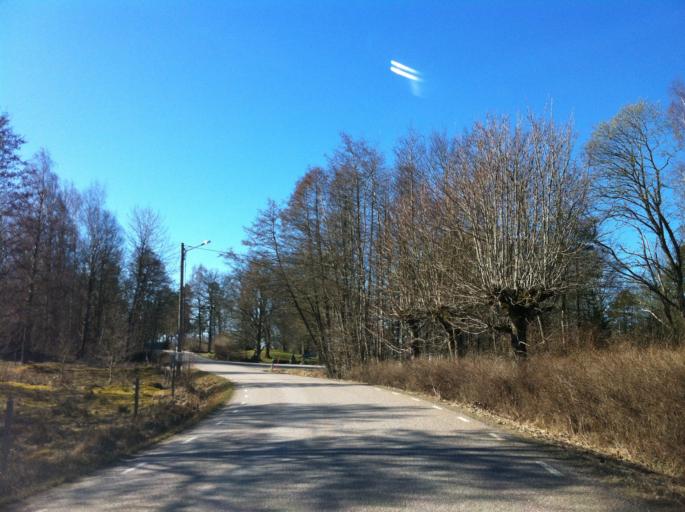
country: SE
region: Vaestra Goetaland
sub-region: Grastorps Kommun
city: Graestorp
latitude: 58.4340
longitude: 12.6076
